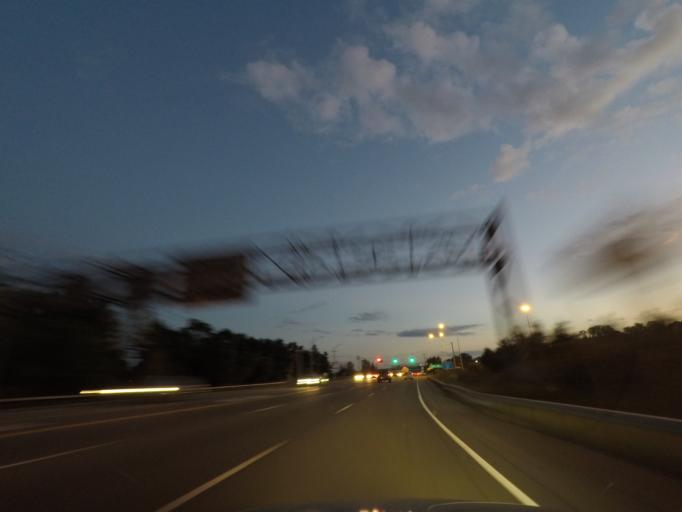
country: US
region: New York
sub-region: Orange County
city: Gardnertown
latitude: 41.5118
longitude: -74.0668
